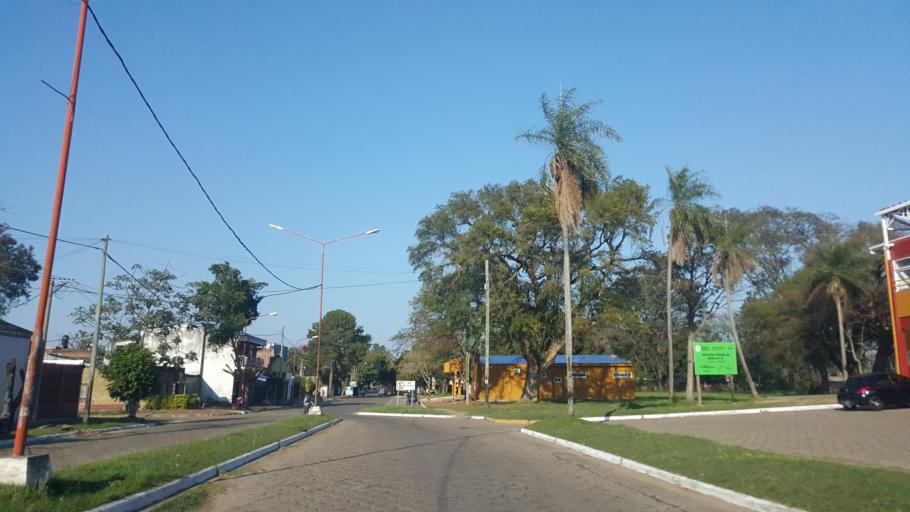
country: AR
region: Corrientes
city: Ituzaingo
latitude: -27.5807
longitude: -56.6831
